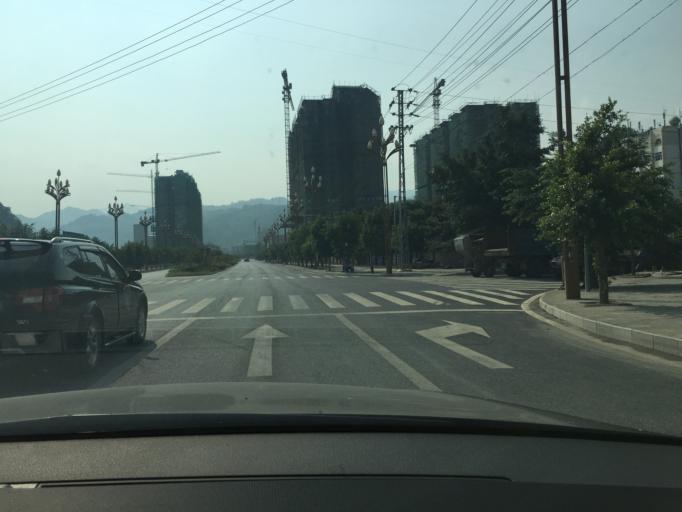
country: CN
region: Guangxi Zhuangzu Zizhiqu
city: Xinzhou
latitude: 24.9946
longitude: 105.7944
